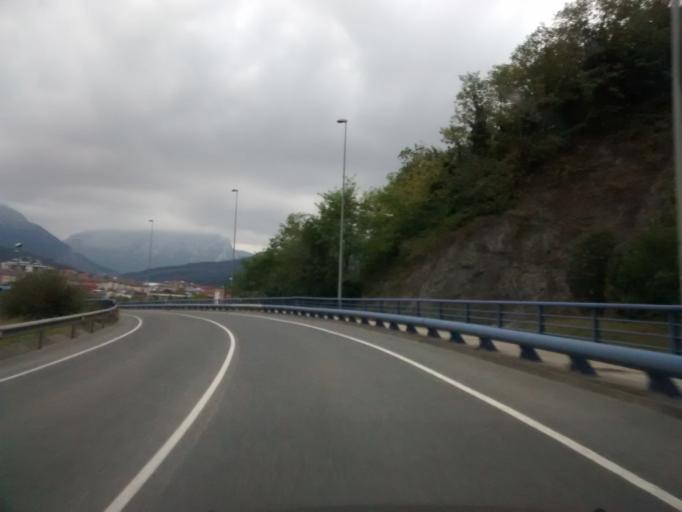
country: ES
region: Basque Country
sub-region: Bizkaia
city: Durango
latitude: 43.1732
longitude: -2.6182
